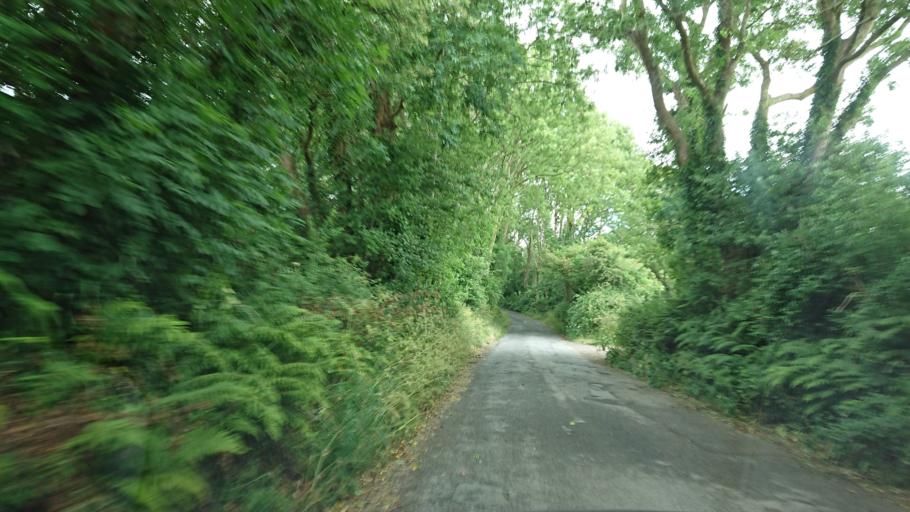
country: IE
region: Munster
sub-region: Waterford
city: Waterford
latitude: 52.2216
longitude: -7.1202
